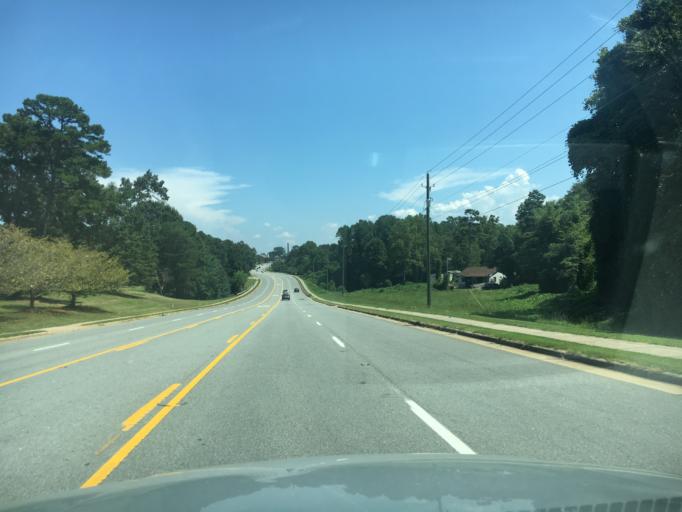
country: US
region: North Carolina
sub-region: Rutherford County
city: Forest City
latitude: 35.3331
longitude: -81.8796
